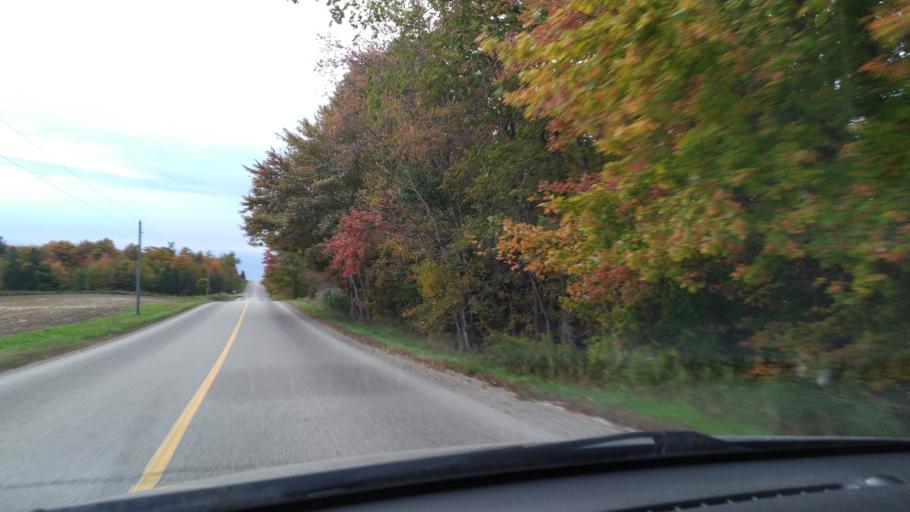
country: CA
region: Ontario
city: Waterloo
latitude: 43.5088
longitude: -80.7031
